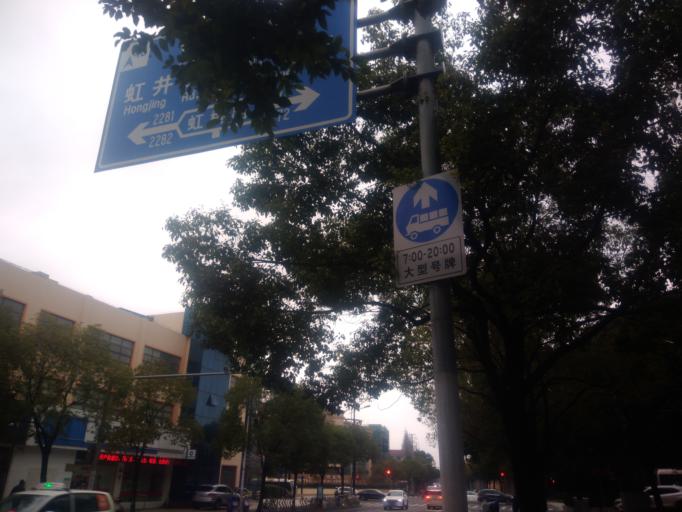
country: CN
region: Shanghai Shi
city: Changzheng
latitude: 31.1929
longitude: 121.3711
